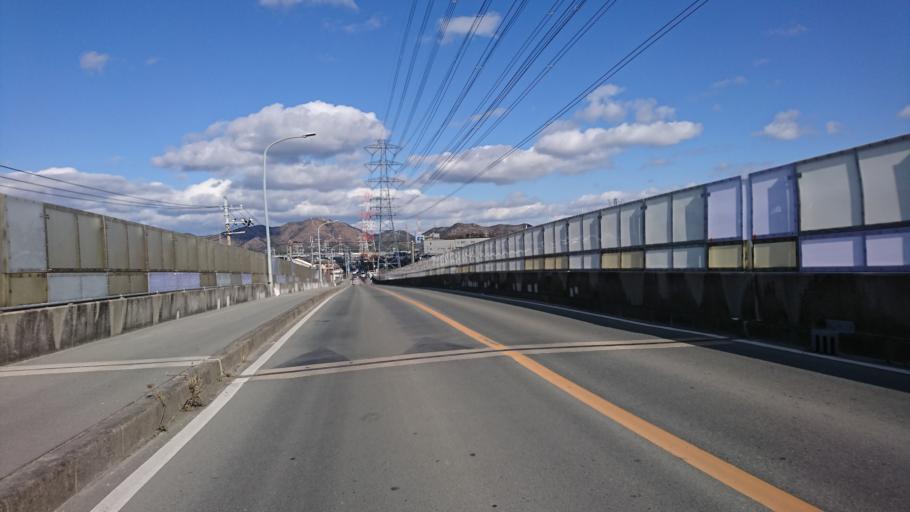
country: JP
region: Hyogo
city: Kakogawacho-honmachi
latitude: 34.7740
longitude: 134.7776
